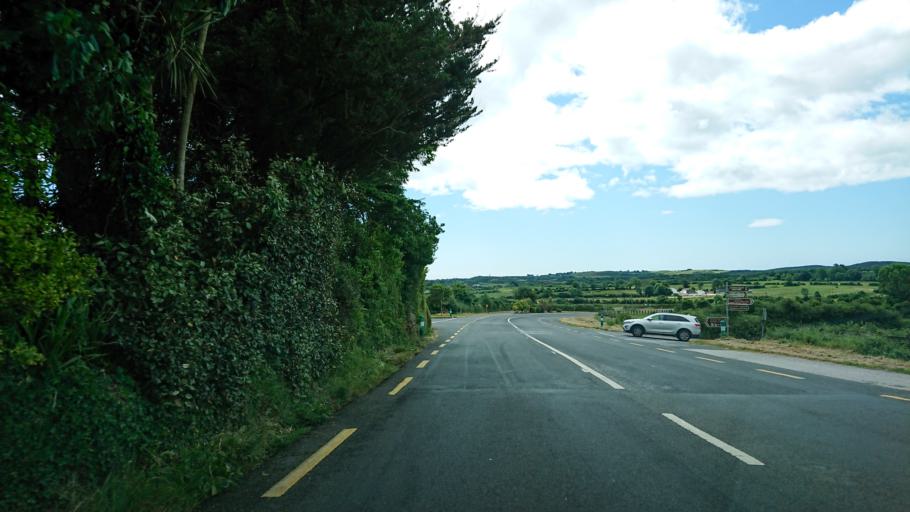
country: IE
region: Munster
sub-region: Waterford
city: Tra Mhor
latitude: 52.1993
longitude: -7.1935
